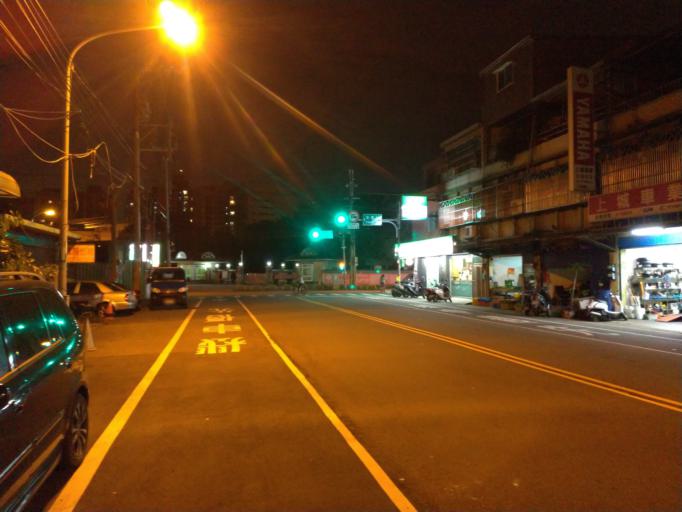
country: TW
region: Taiwan
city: Taoyuan City
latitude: 24.9726
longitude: 121.2473
